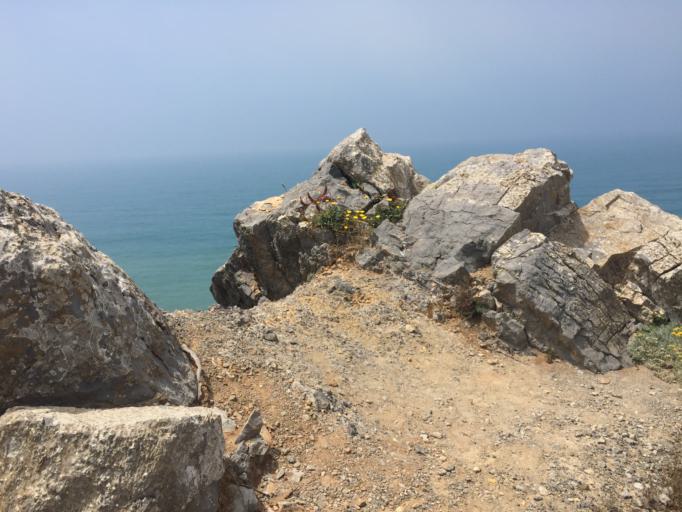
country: PT
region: Lisbon
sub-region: Sintra
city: Colares
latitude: 38.8079
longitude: -9.4831
